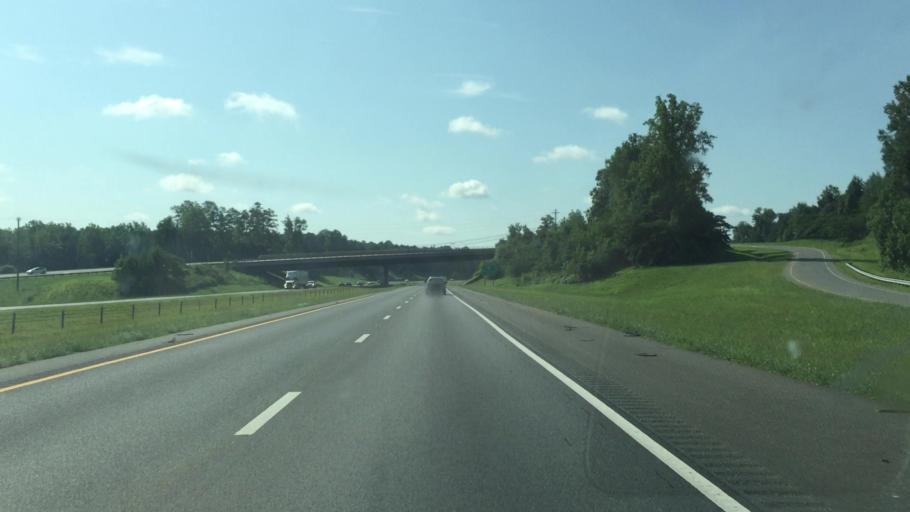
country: US
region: North Carolina
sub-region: Mecklenburg County
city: Mint Hill
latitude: 35.2040
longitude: -80.6354
